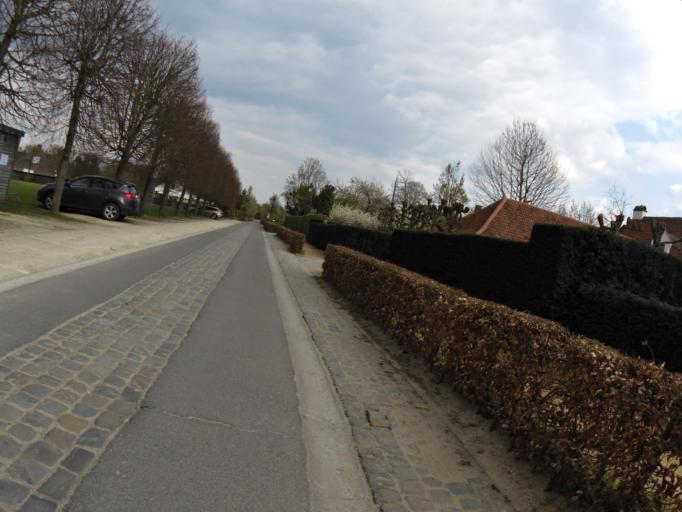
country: BE
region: Flanders
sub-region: Provincie Oost-Vlaanderen
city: Sint-Martens-Latem
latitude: 51.0197
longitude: 3.6417
